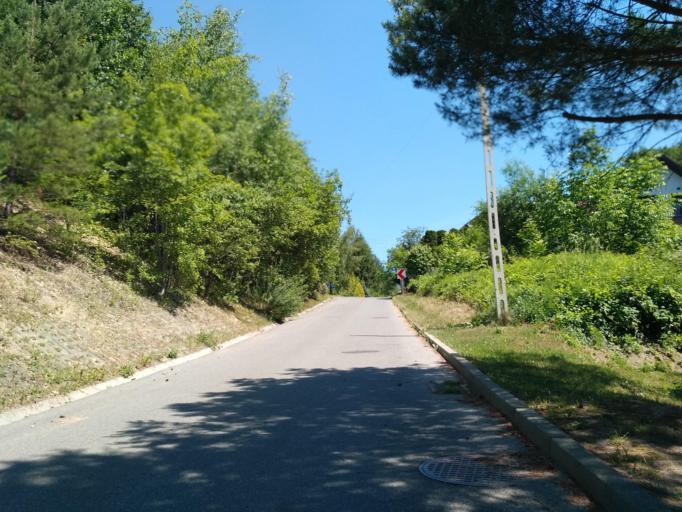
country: PL
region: Subcarpathian Voivodeship
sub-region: Krosno
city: Krosno
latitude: 49.7028
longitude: 21.7707
